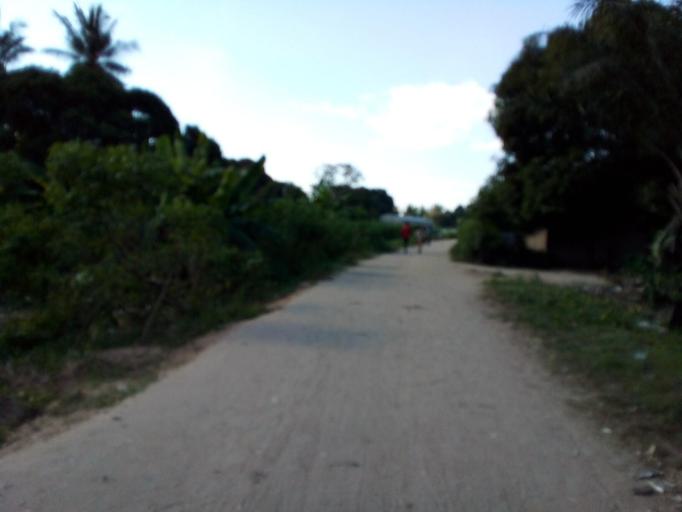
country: MZ
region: Zambezia
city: Quelimane
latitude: -17.6037
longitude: 36.8216
